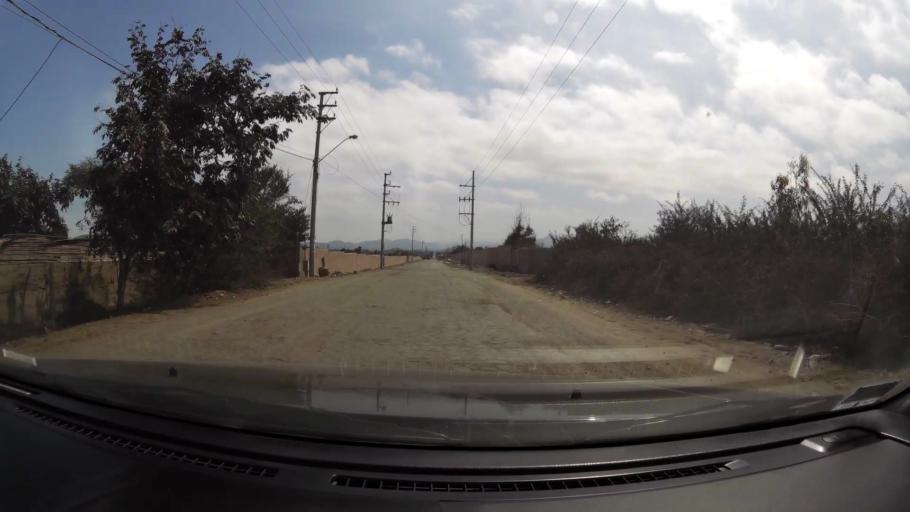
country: PE
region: Lima
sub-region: Provincia de Canete
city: Mala
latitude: -12.7159
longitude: -76.6191
